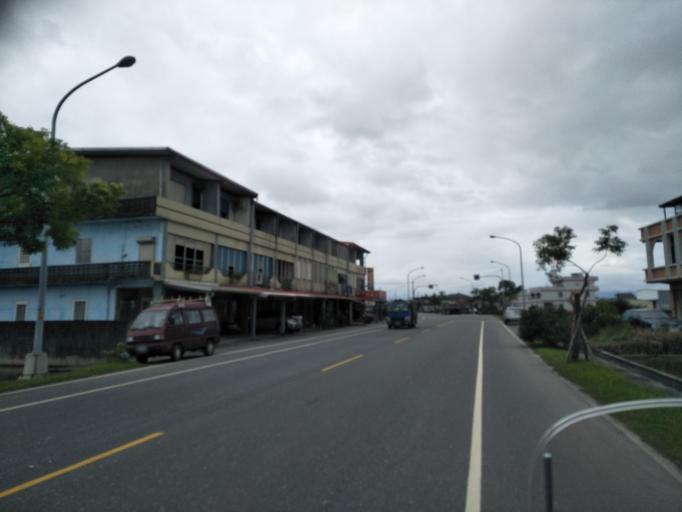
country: TW
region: Taiwan
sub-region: Yilan
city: Yilan
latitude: 24.7935
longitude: 121.7849
